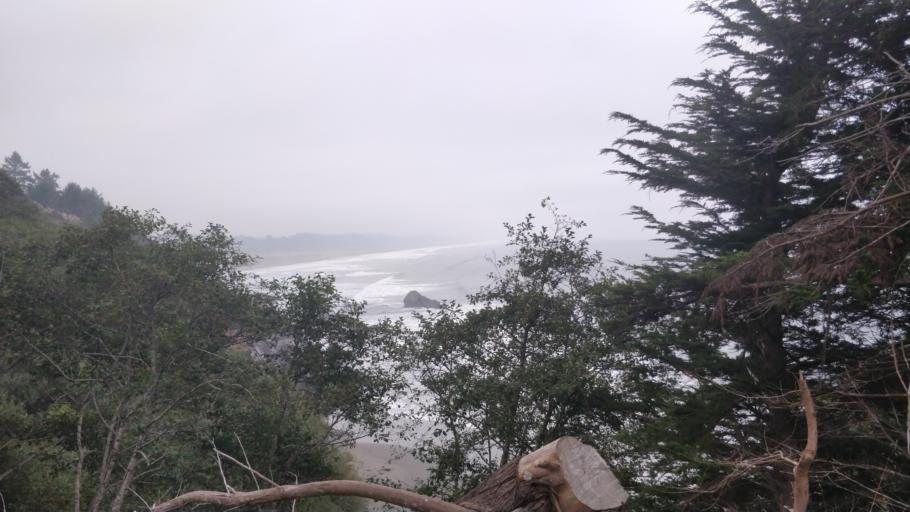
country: US
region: California
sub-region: Humboldt County
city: Westhaven-Moonstone
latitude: 41.0364
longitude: -124.1178
